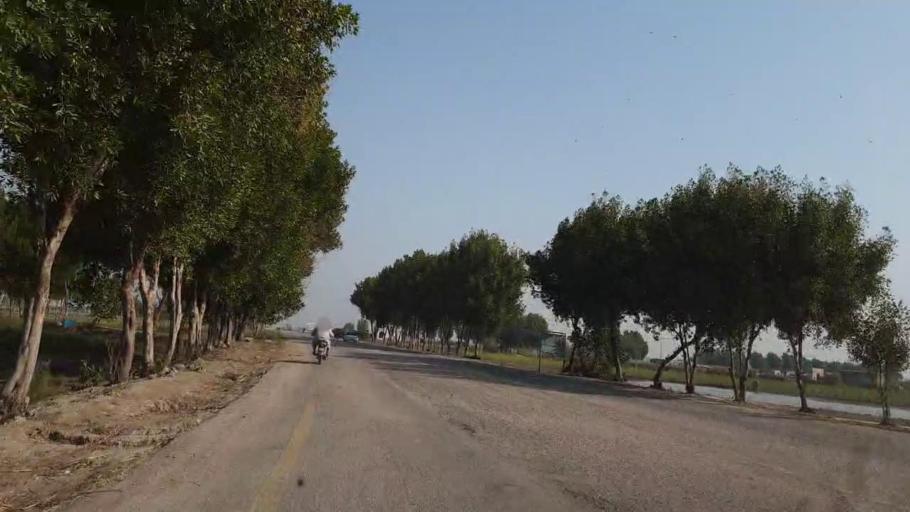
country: PK
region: Sindh
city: Mirpur Khas
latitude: 25.5403
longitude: 69.0459
